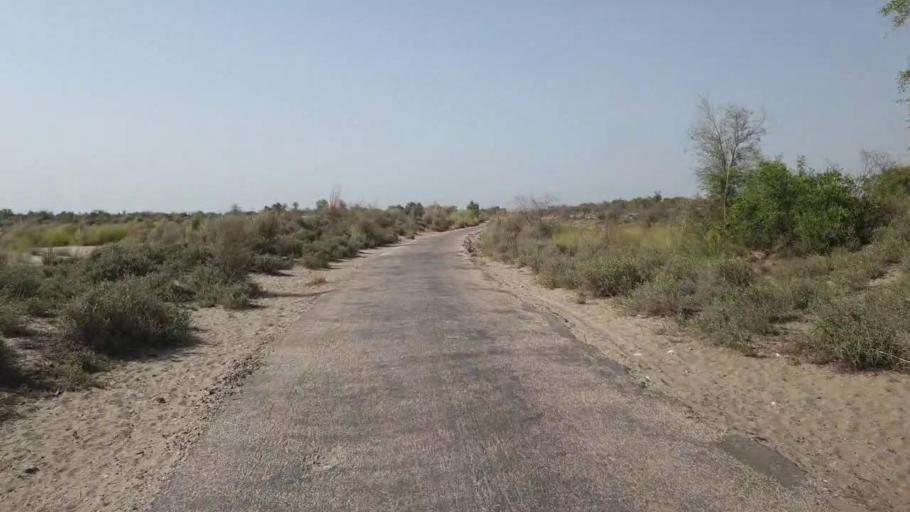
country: PK
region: Sindh
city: Jam Sahib
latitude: 26.5924
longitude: 68.9222
